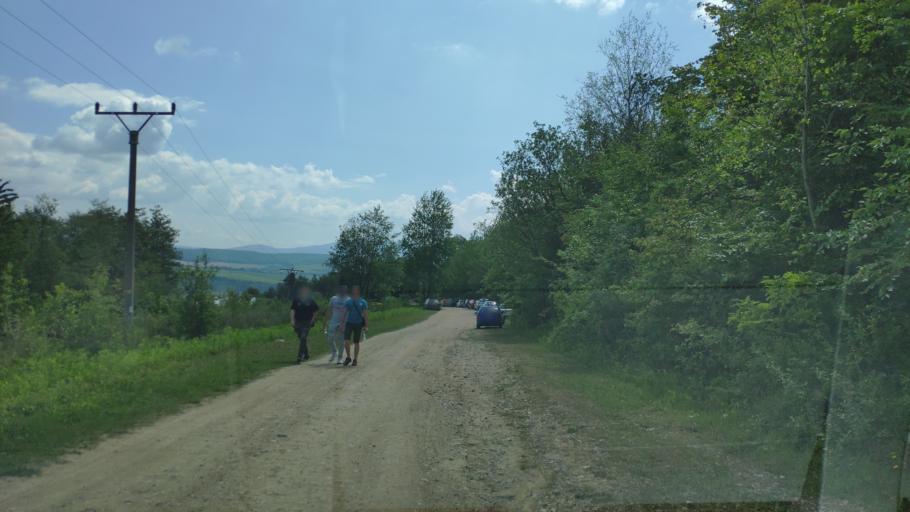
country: SK
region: Kosicky
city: Kosice
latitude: 48.7720
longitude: 21.2974
